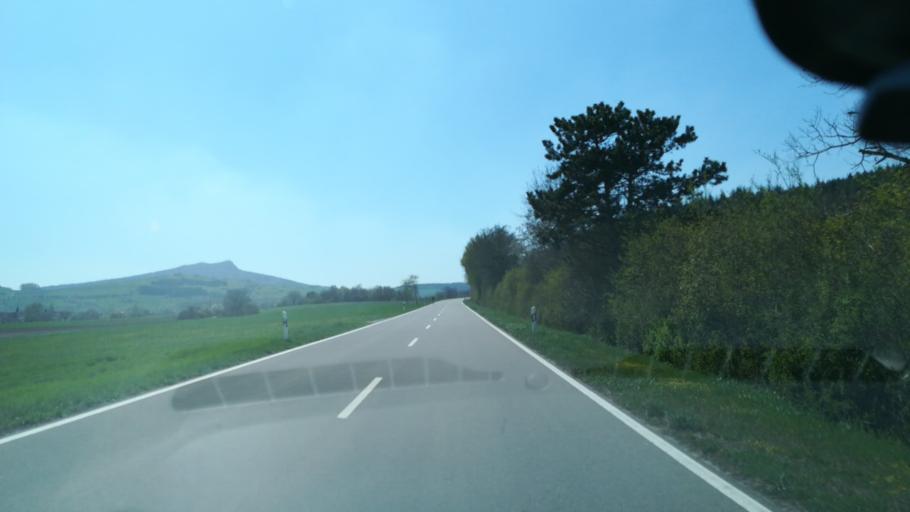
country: DE
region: Baden-Wuerttemberg
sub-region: Freiburg Region
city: Muhlhausen-Ehingen
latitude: 47.8351
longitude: 8.8043
